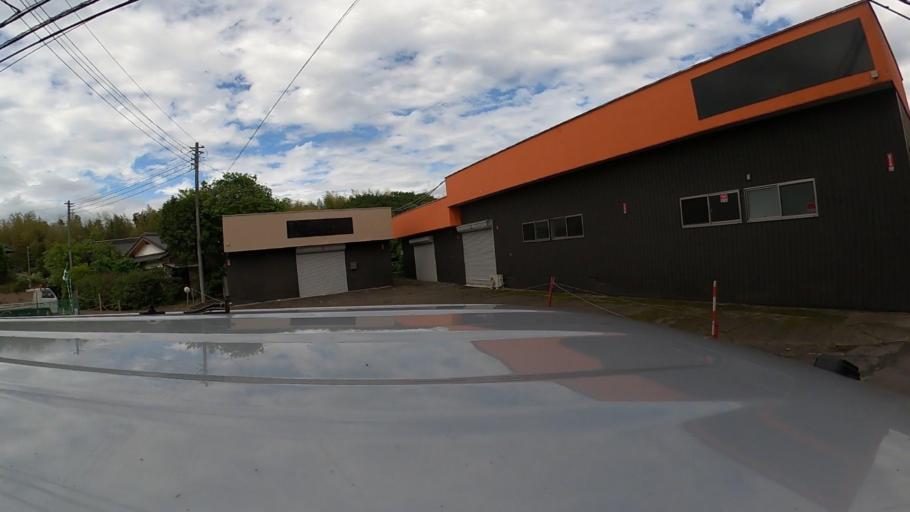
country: JP
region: Ibaraki
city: Ushiku
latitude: 35.9776
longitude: 140.1751
